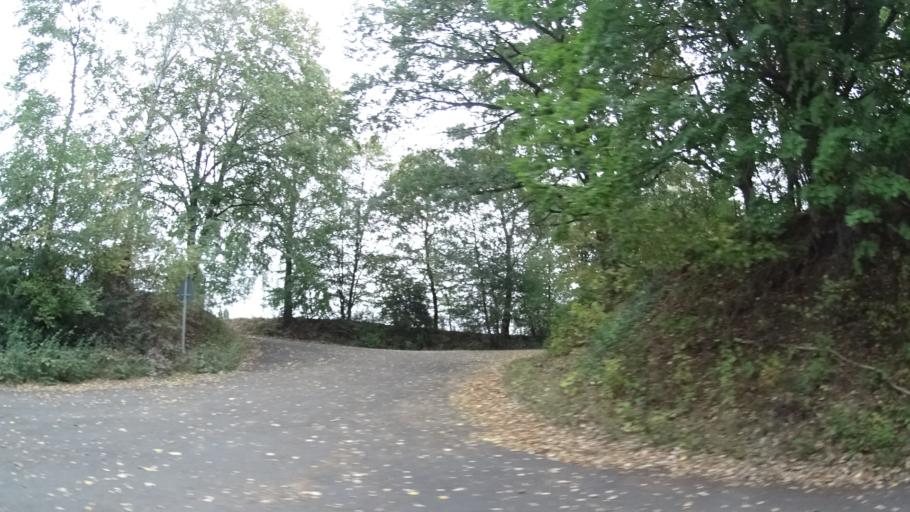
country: DE
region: Hesse
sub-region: Regierungsbezirk Kassel
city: Dipperz
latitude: 50.4849
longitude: 9.8059
